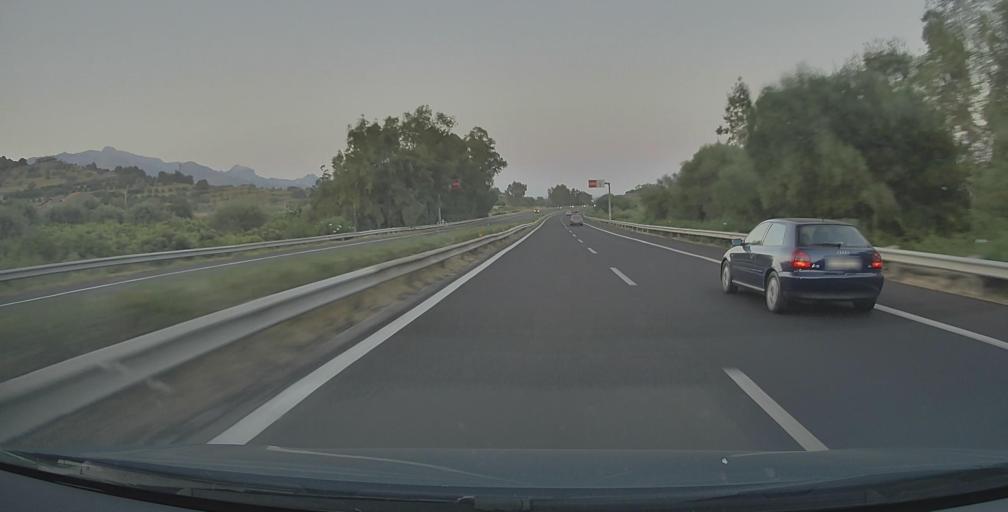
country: IT
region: Sicily
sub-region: Catania
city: Pasteria-Lapide
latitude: 37.8154
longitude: 15.2191
